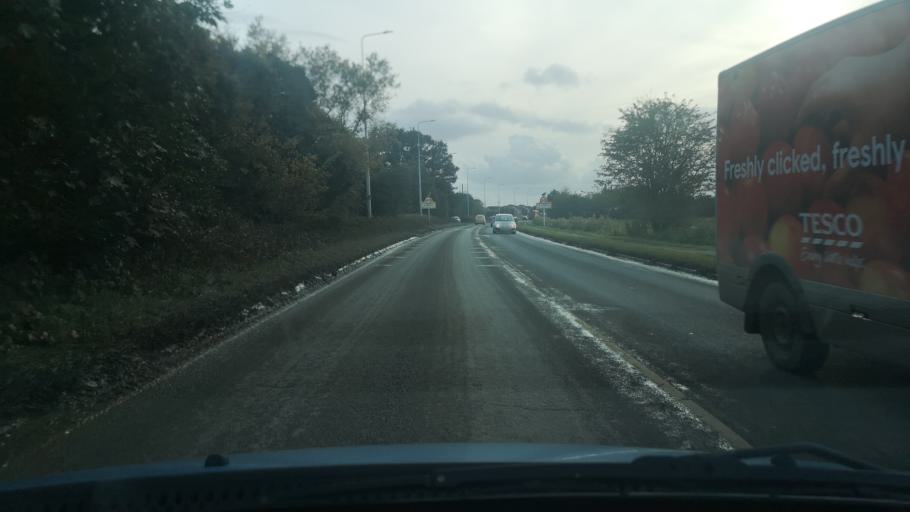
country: GB
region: England
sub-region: North Lincolnshire
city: Gunness
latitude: 53.5809
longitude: -0.7394
